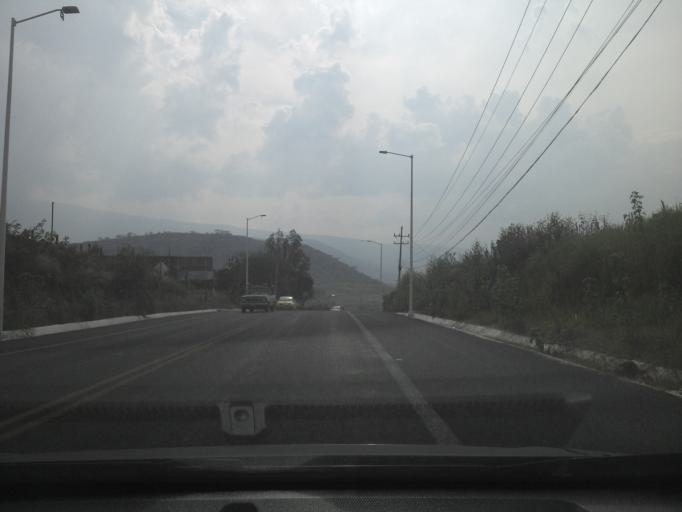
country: MX
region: Jalisco
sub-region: Tlajomulco de Zuniga
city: Lomas del Sur
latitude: 20.4862
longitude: -103.4277
